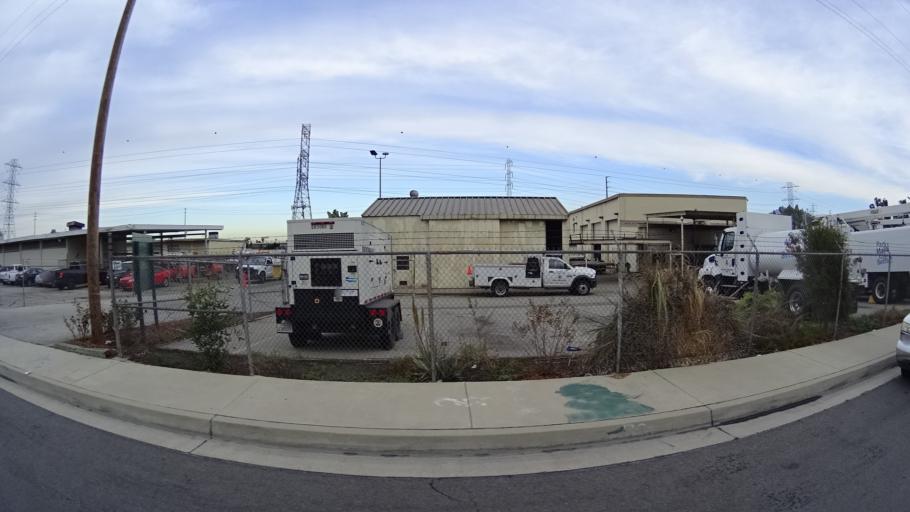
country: US
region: California
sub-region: Los Angeles County
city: Avocado Heights
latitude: 34.0575
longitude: -118.0030
